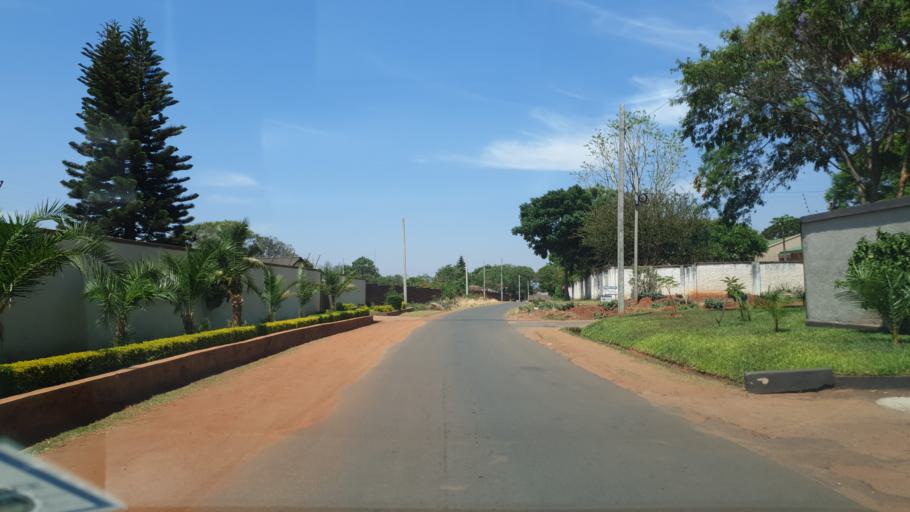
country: MW
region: Central Region
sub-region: Lilongwe District
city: Lilongwe
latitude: -13.9810
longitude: 33.7491
